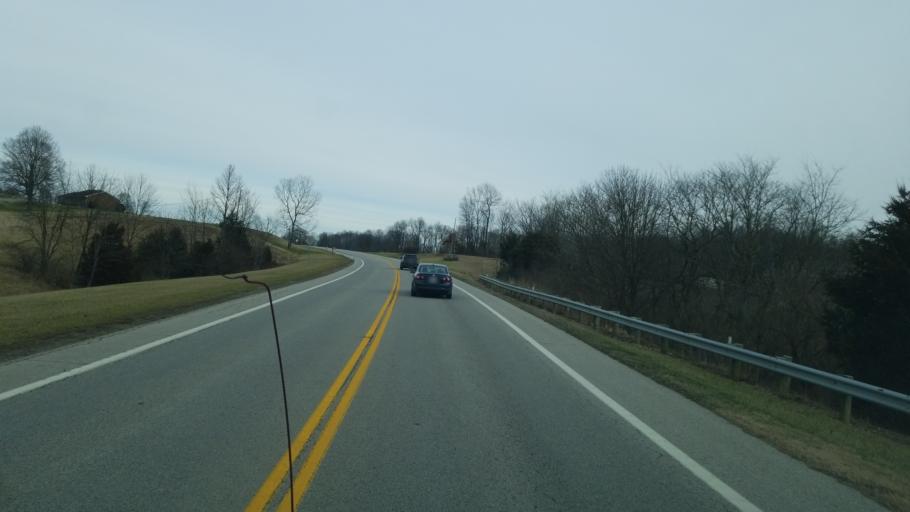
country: US
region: Ohio
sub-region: Highland County
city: Hillsboro
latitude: 39.1628
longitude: -83.6381
